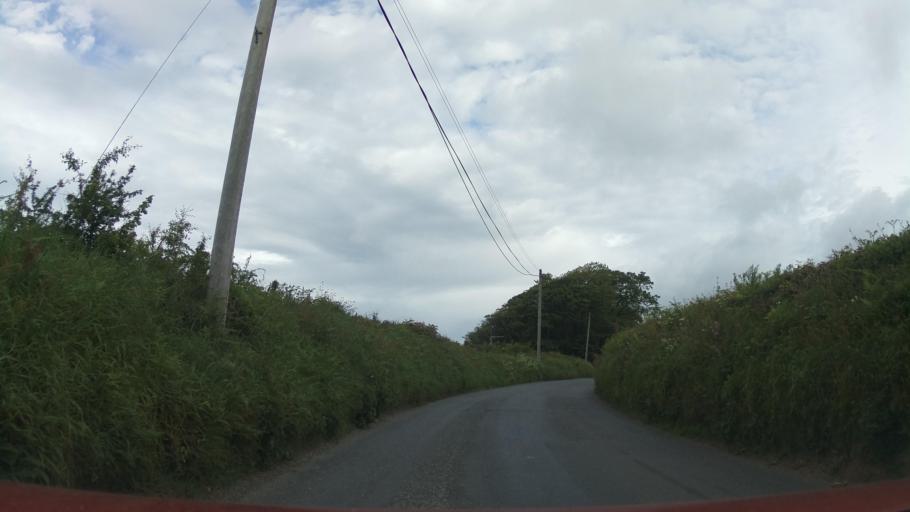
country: GB
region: England
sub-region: Devon
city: Dartmouth
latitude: 50.3510
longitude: -3.6603
